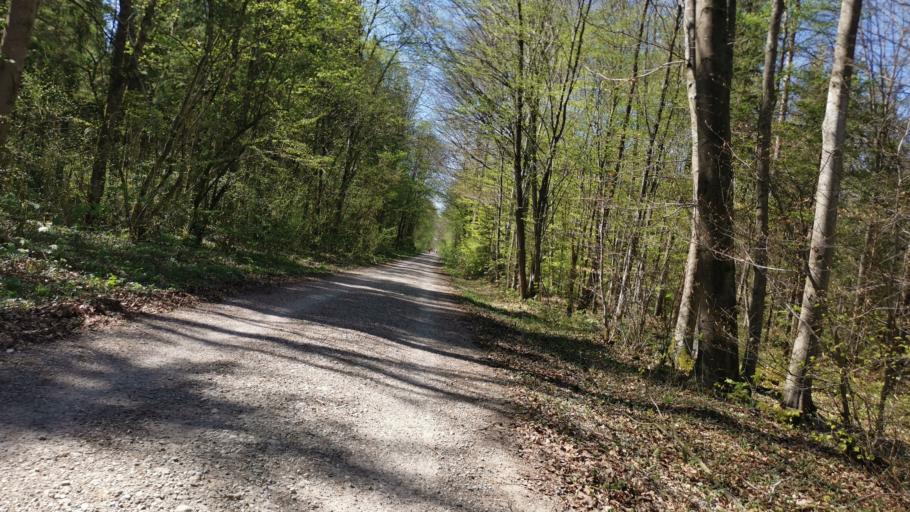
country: DE
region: Bavaria
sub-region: Upper Bavaria
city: Neuried
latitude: 48.0872
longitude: 11.4441
